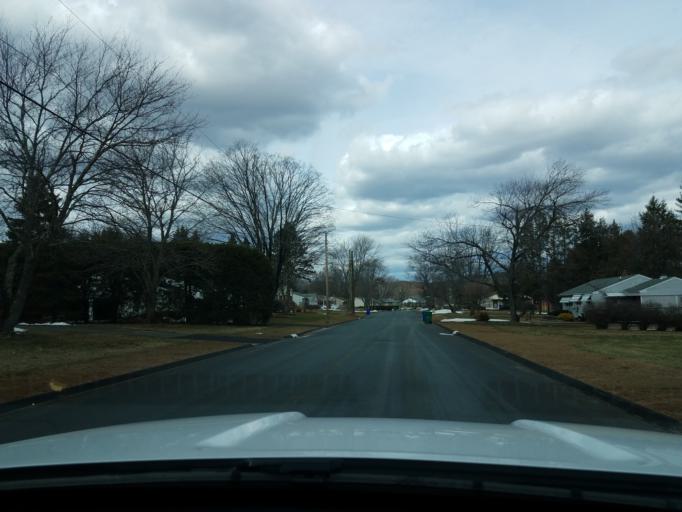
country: US
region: Connecticut
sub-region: Hartford County
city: Manchester
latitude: 41.8229
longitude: -72.5176
